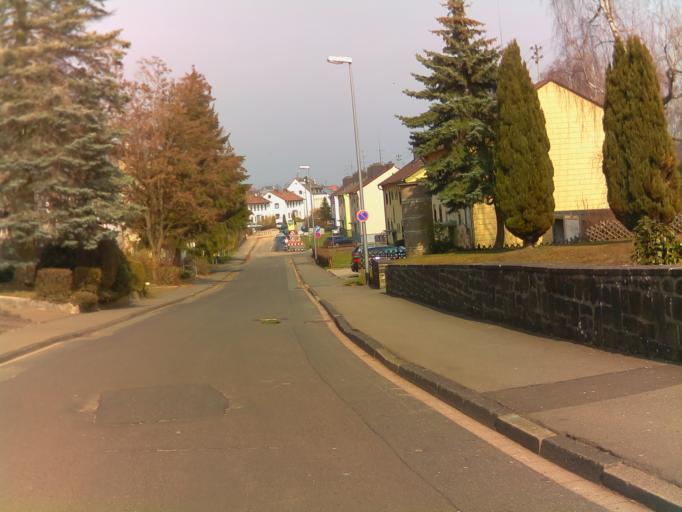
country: DE
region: Rheinland-Pfalz
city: Baumholder
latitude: 49.6062
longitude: 7.3314
